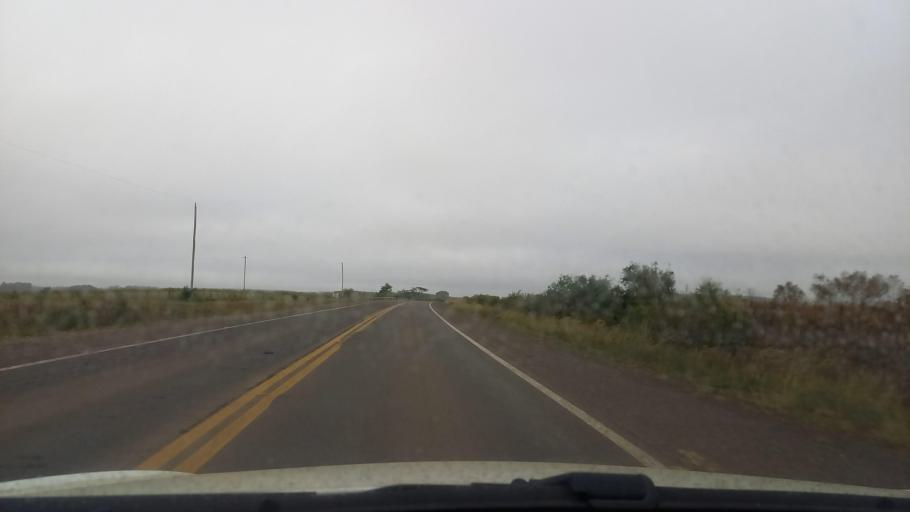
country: BR
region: Rio Grande do Sul
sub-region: Rosario Do Sul
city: Rosario do Sul
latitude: -30.1397
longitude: -54.6653
